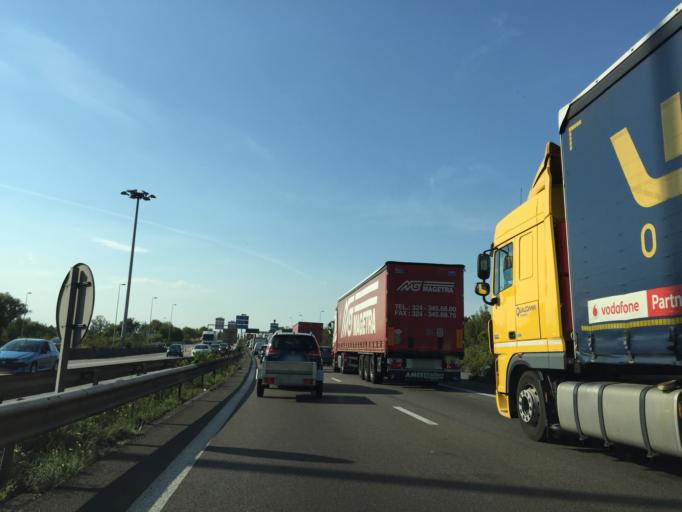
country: FR
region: Alsace
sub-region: Departement du Bas-Rhin
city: Strasbourg
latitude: 48.5748
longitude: 7.7292
